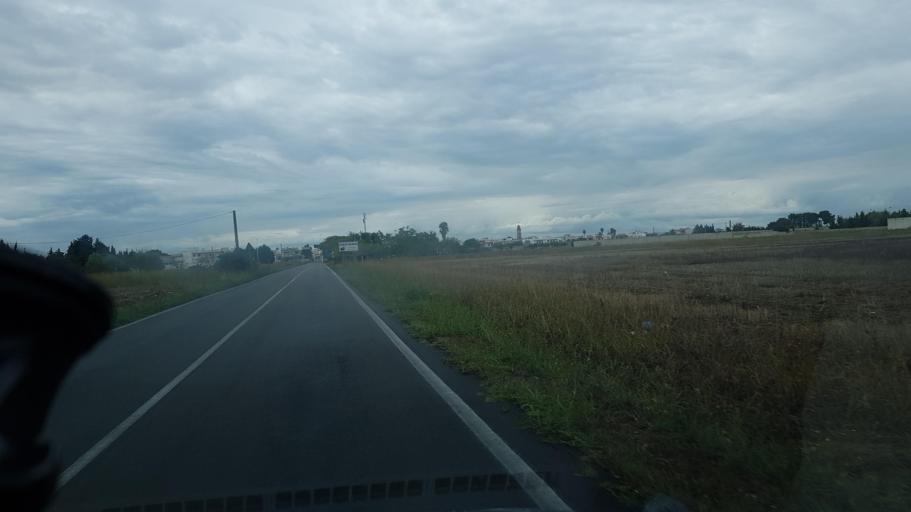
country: IT
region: Apulia
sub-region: Provincia di Lecce
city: Salice Salentino
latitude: 40.3792
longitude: 17.9739
